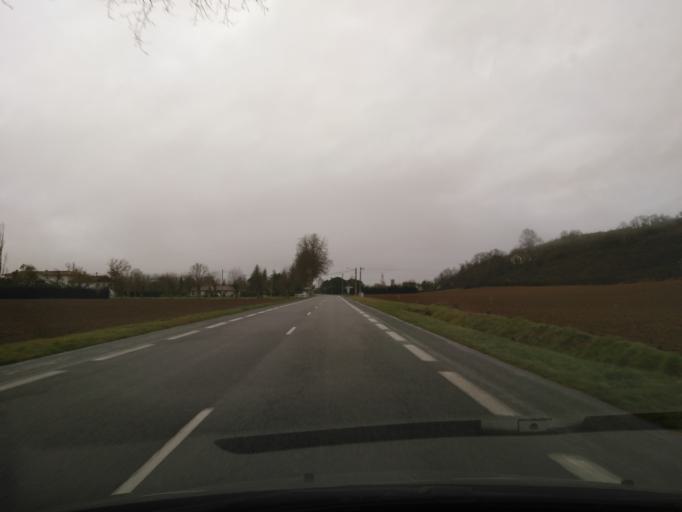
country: FR
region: Midi-Pyrenees
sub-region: Departement de la Haute-Garonne
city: Rieux-Volvestre
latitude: 43.2474
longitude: 1.2023
